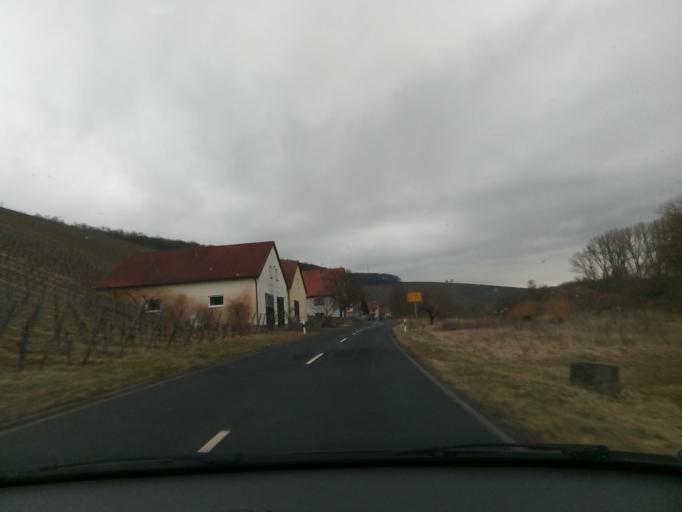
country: DE
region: Bavaria
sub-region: Regierungsbezirk Unterfranken
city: Nordheim
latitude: 49.8454
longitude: 10.1688
